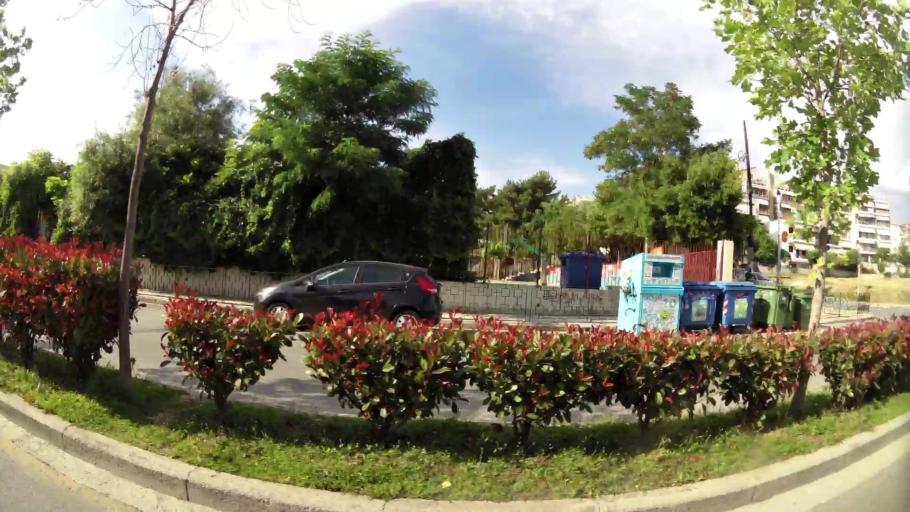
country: GR
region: Central Macedonia
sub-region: Nomos Thessalonikis
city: Kalamaria
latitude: 40.5760
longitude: 22.9634
